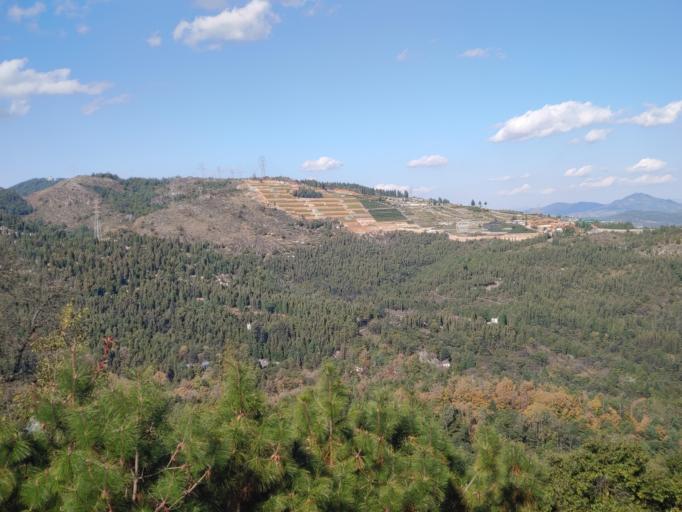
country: CN
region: Yunnan
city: Majie
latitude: 25.0664
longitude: 102.6230
